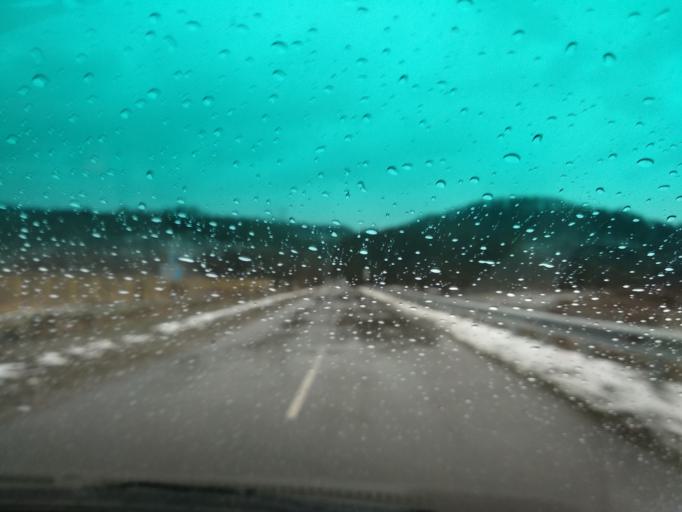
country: RU
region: Krasnodarskiy
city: Khadyzhensk
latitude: 44.2203
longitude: 39.3935
